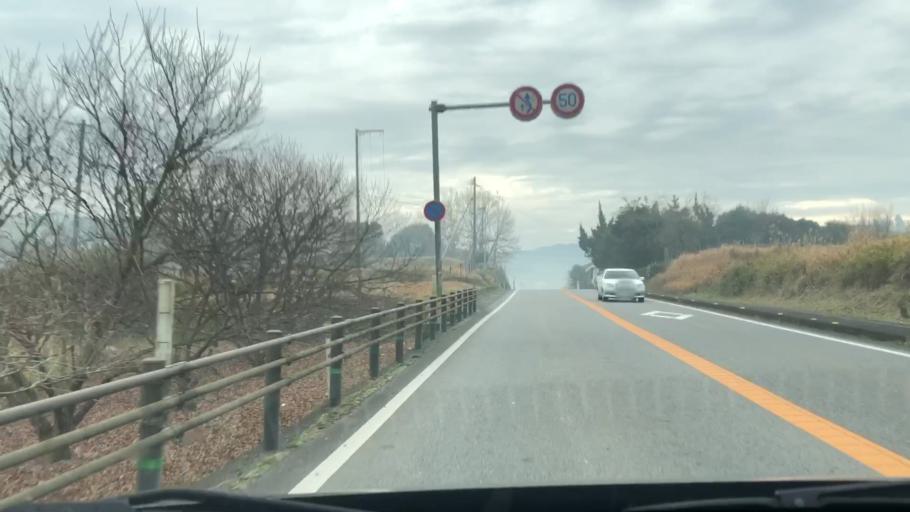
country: JP
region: Oita
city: Usuki
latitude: 33.0214
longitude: 131.6966
